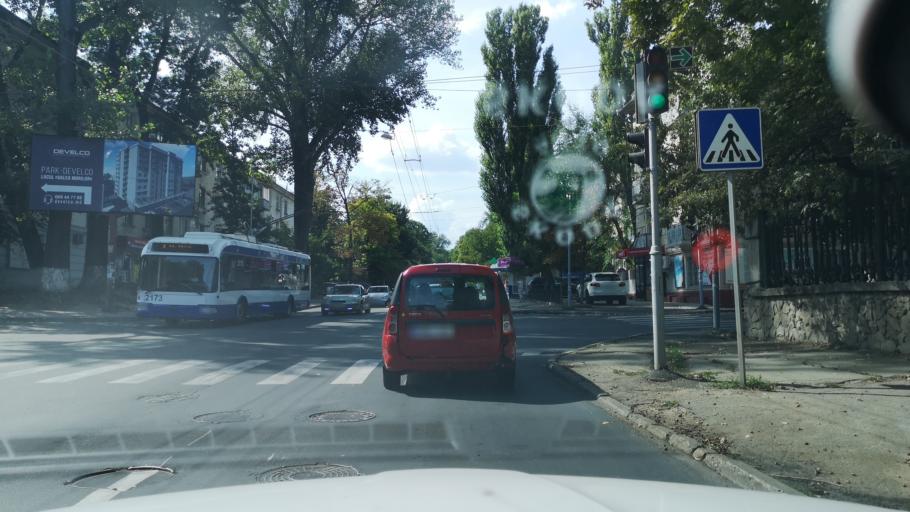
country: MD
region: Chisinau
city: Chisinau
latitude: 47.0223
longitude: 28.8098
